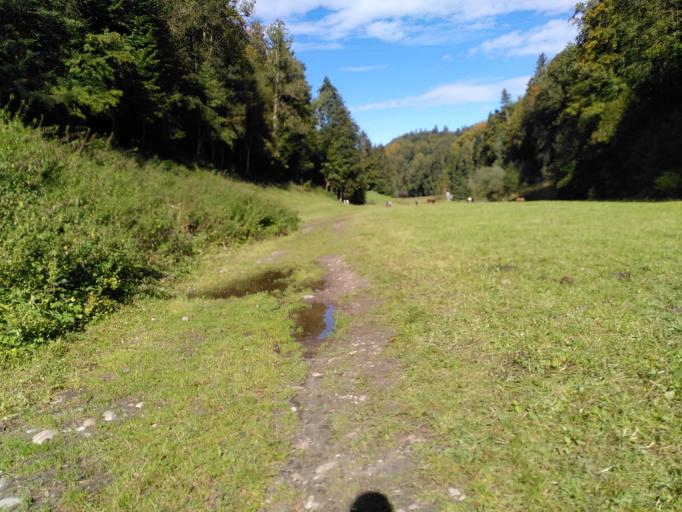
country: CH
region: Bern
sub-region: Oberaargau
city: Seeberg
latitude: 47.1321
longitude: 7.7035
